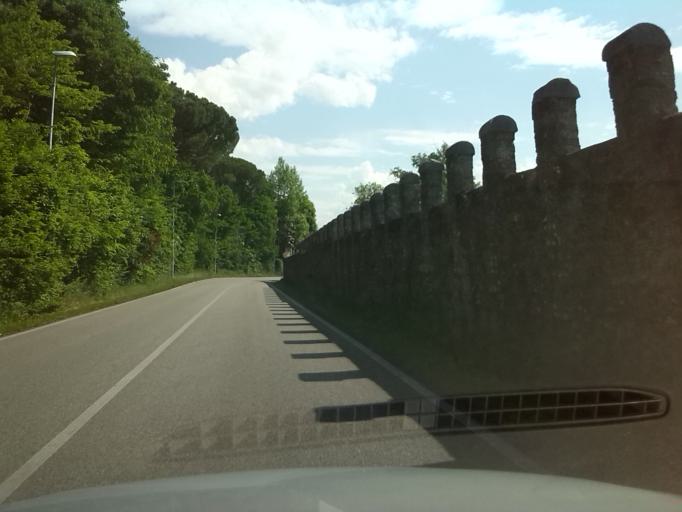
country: IT
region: Friuli Venezia Giulia
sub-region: Provincia di Udine
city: San Giovanni al Natisone
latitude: 45.9843
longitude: 13.4208
